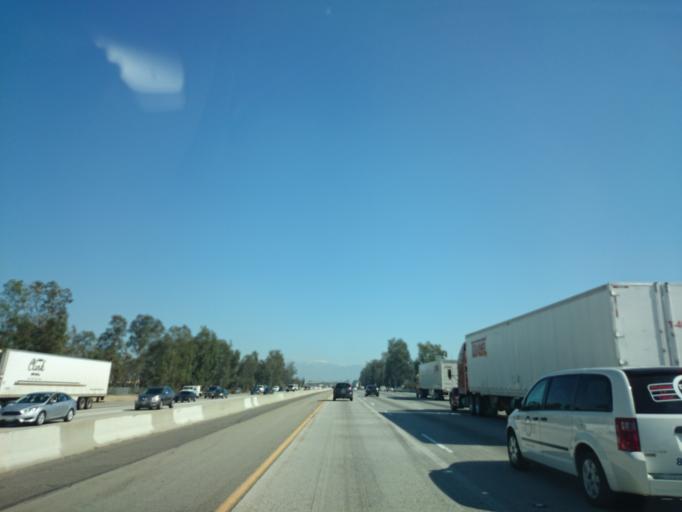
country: US
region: California
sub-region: San Bernardino County
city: Fontana
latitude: 34.0664
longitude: -117.4657
